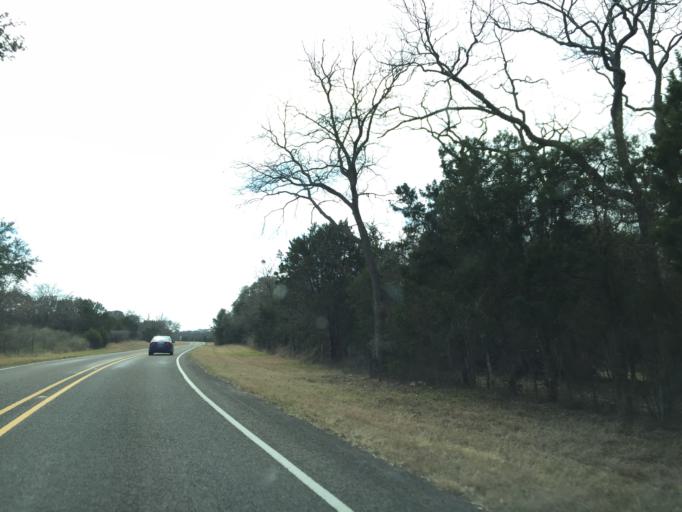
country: US
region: Texas
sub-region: Burnet County
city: Granite Shoals
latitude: 30.5095
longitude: -98.4402
